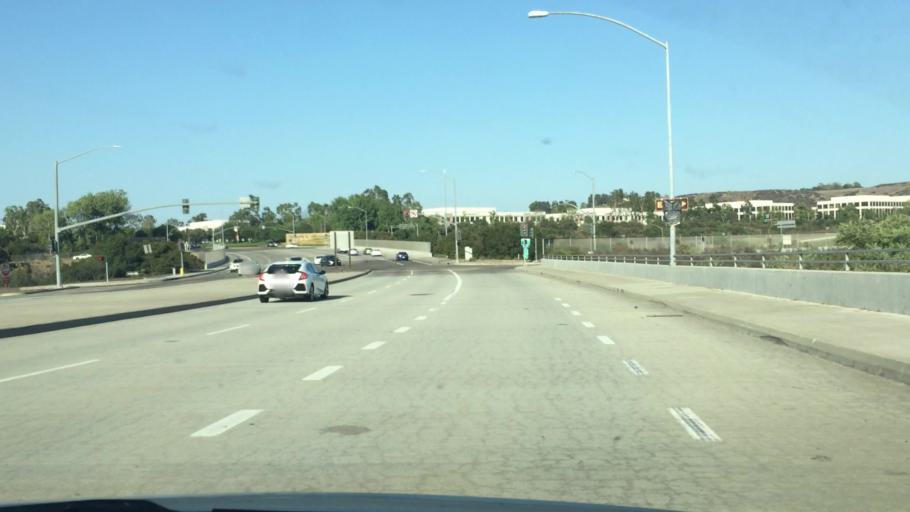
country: US
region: California
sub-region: Orange County
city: San Joaquin Hills
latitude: 33.6371
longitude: -117.8585
